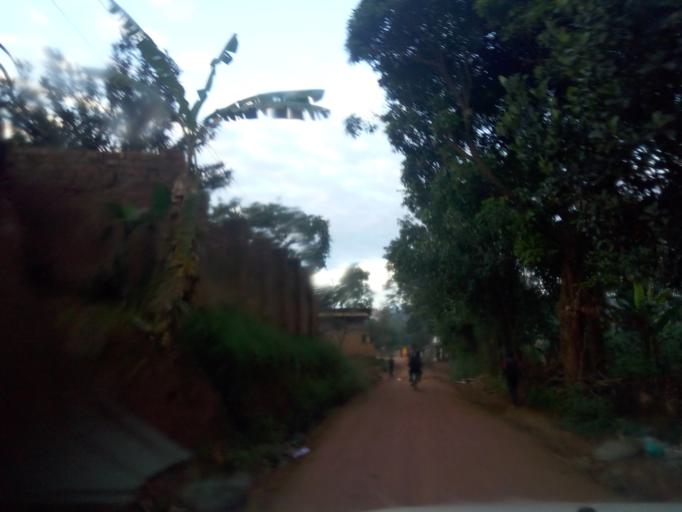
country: UG
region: Central Region
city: Kampala Central Division
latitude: 0.3843
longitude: 32.5638
